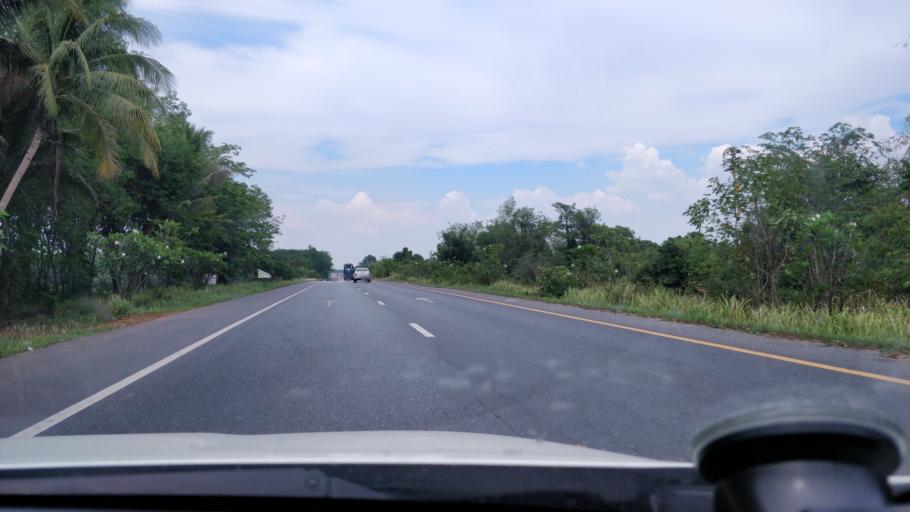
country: TH
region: Surat Thani
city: Khian Sa
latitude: 8.8989
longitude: 99.2309
